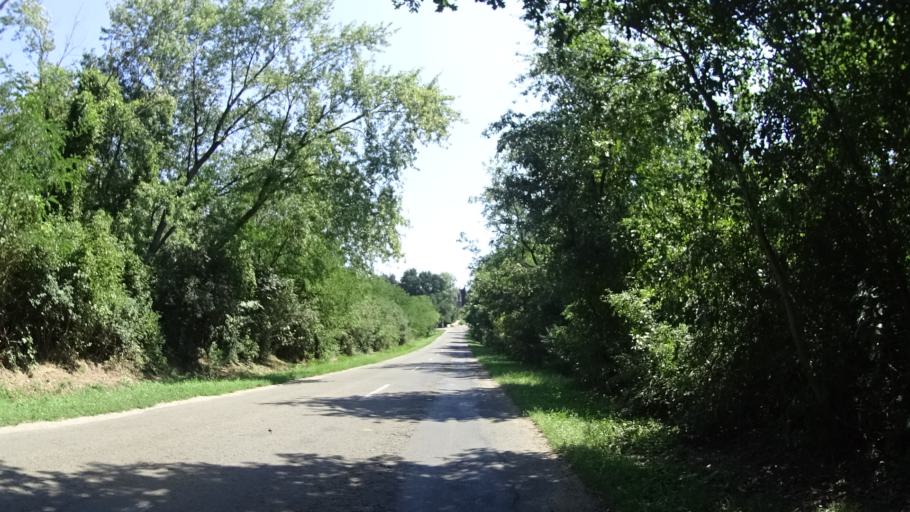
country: HU
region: Fejer
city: Pakozd
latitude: 47.2250
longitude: 18.5764
